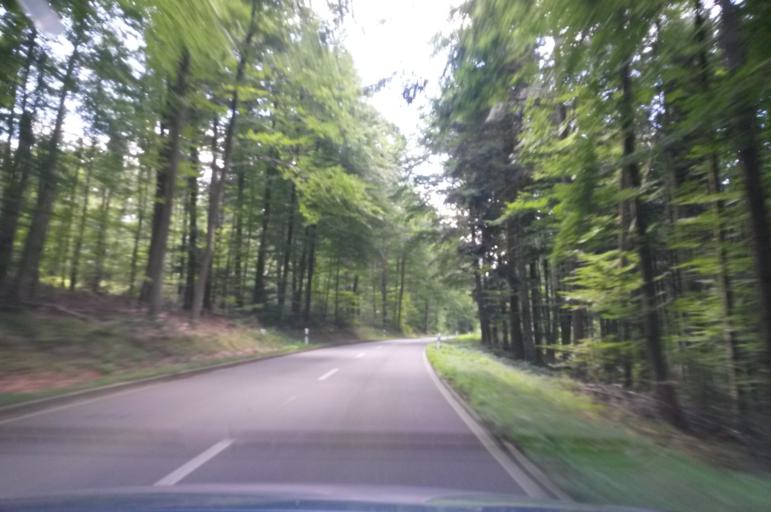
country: DE
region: Baden-Wuerttemberg
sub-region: Karlsruhe Region
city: Bad Herrenalb
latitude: 48.8518
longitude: 8.4443
